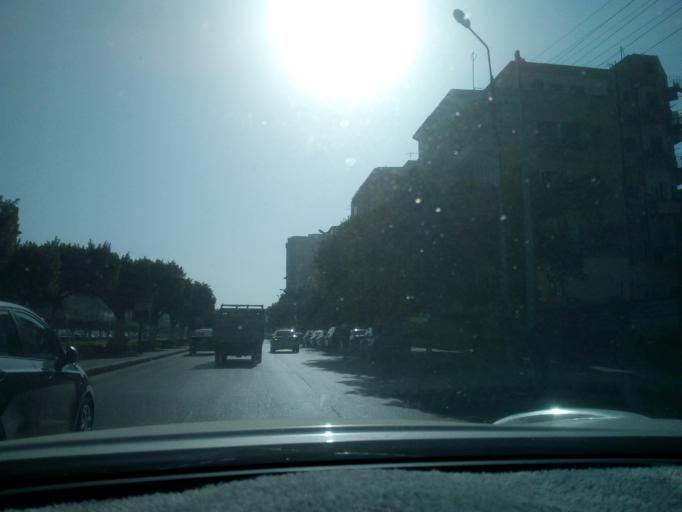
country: EG
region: Muhafazat al Qahirah
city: Cairo
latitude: 30.1025
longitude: 31.3302
